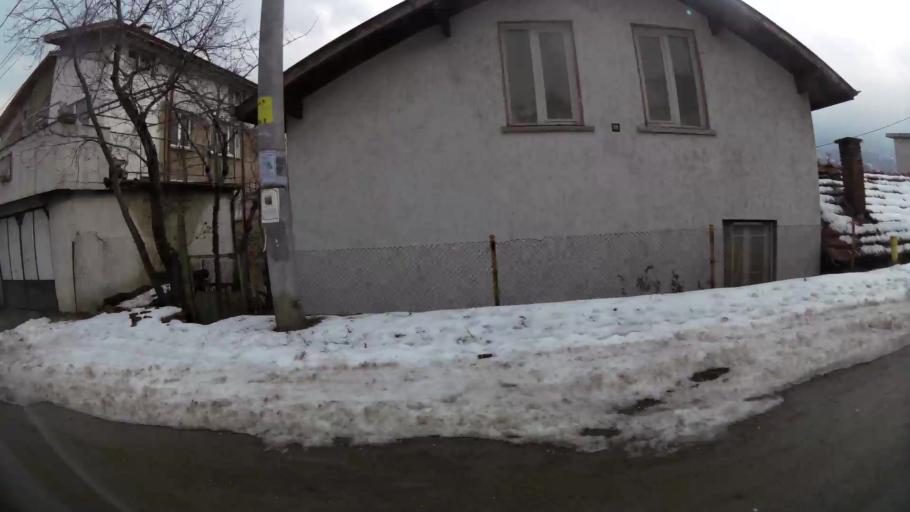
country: BG
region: Sofia-Capital
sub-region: Stolichna Obshtina
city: Sofia
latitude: 42.6598
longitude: 23.2382
